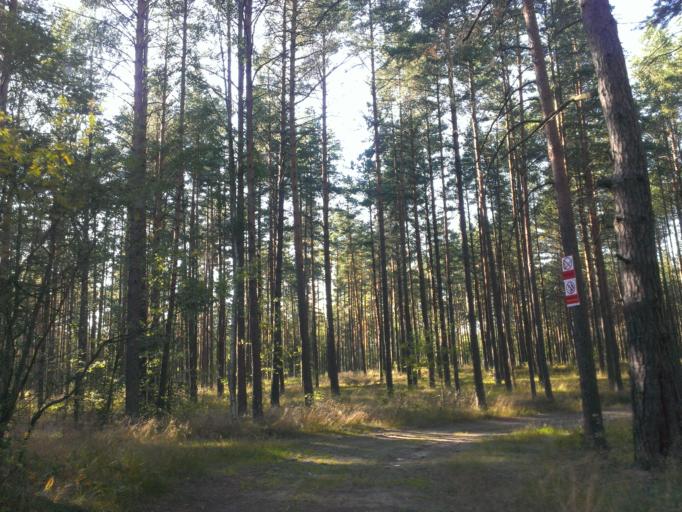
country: LV
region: Riga
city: Jaunciems
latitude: 57.0470
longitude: 24.2433
